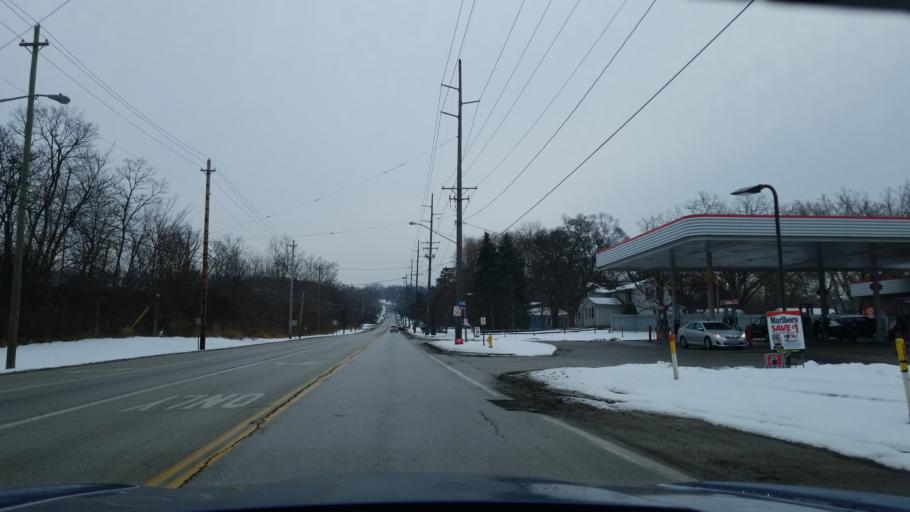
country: US
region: Ohio
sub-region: Cuyahoga County
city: North Royalton
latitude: 41.3128
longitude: -81.7552
